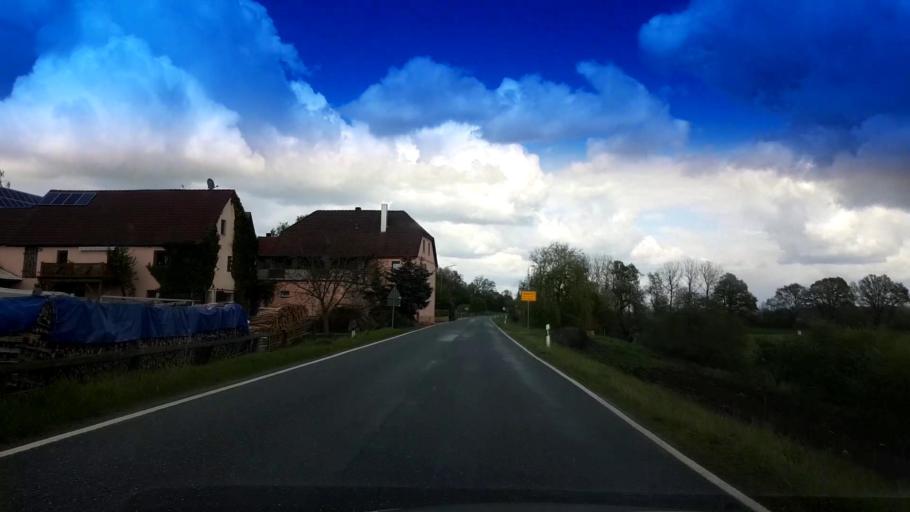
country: DE
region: Bavaria
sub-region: Upper Franconia
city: Frensdorf
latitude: 49.7889
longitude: 10.8733
